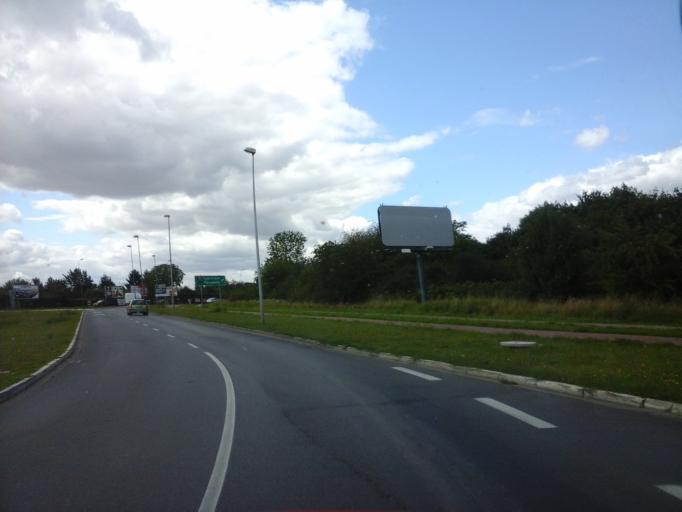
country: PL
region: West Pomeranian Voivodeship
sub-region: Powiat policki
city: Przeclaw
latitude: 53.4278
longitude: 14.4817
